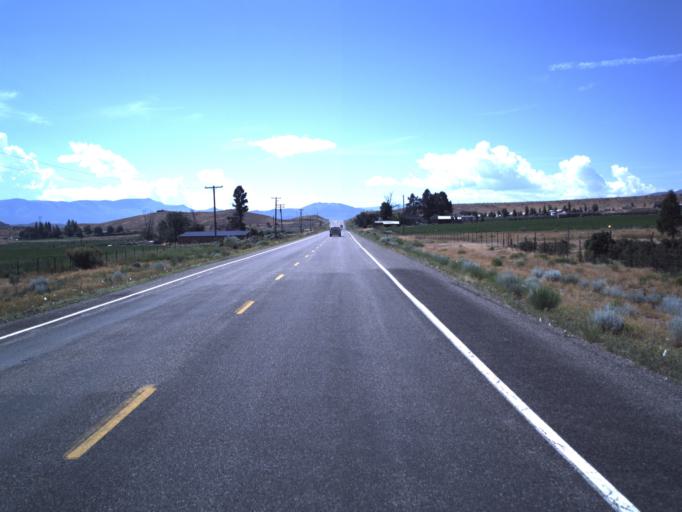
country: US
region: Utah
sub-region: Sevier County
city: Monroe
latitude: 38.4699
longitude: -112.2359
